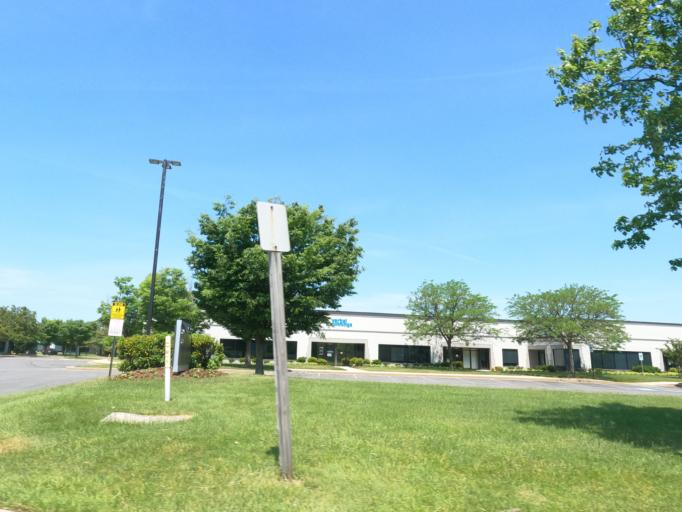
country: US
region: Maryland
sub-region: Anne Arundel County
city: Jessup
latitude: 39.1812
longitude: -76.8059
